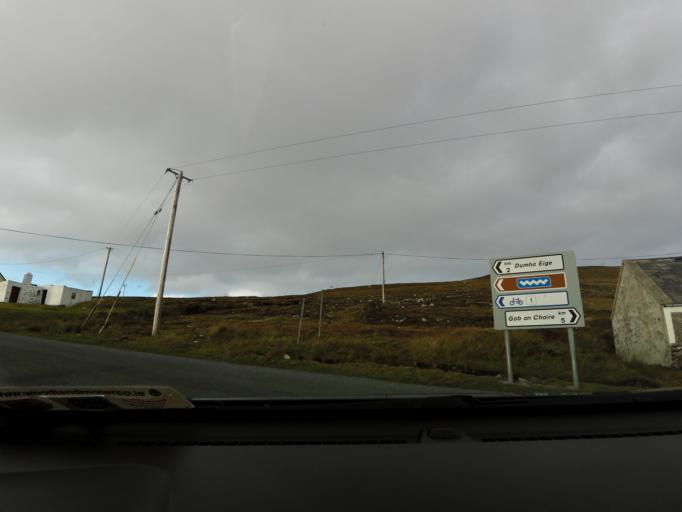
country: IE
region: Connaught
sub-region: Maigh Eo
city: Belmullet
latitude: 53.9066
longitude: -9.9937
